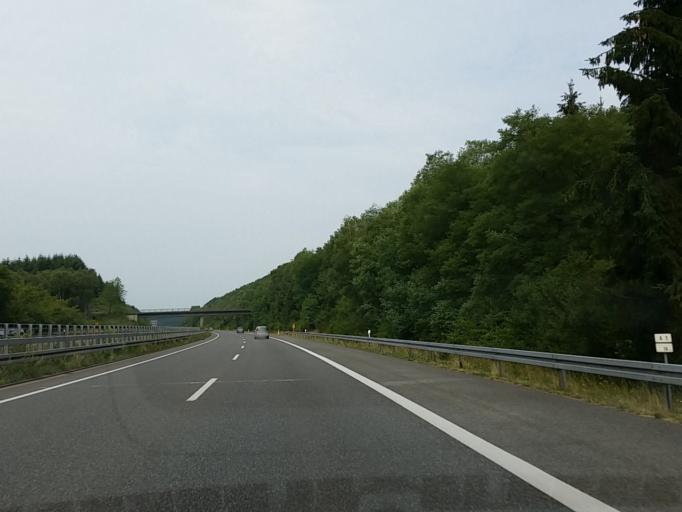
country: DE
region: Saarland
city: Nonnweiler
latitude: 49.6155
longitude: 6.9537
